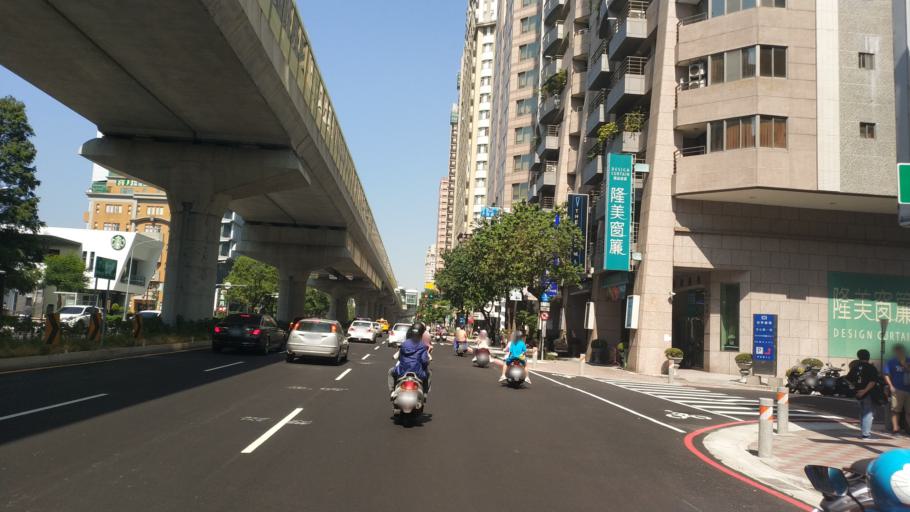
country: TW
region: Taiwan
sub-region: Taichung City
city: Taichung
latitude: 24.1417
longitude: 120.6469
